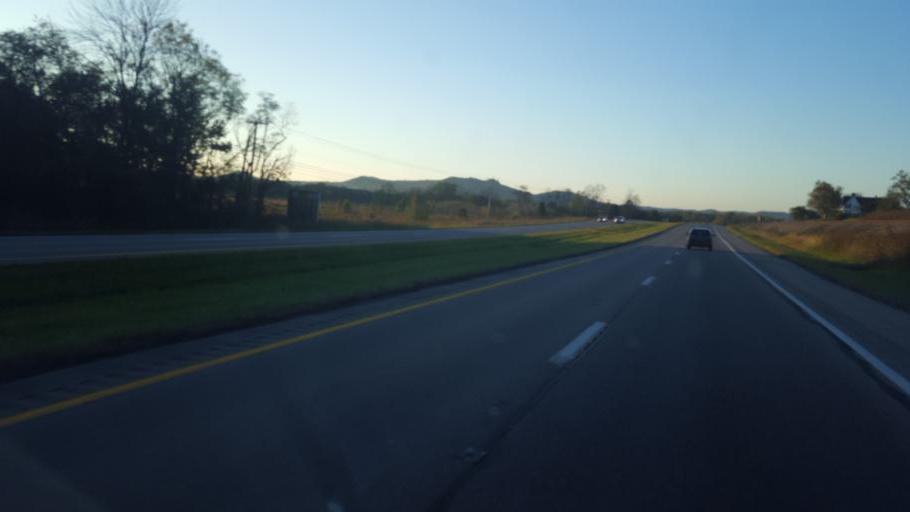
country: US
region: Ohio
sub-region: Scioto County
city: Lucasville
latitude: 38.9172
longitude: -83.0158
